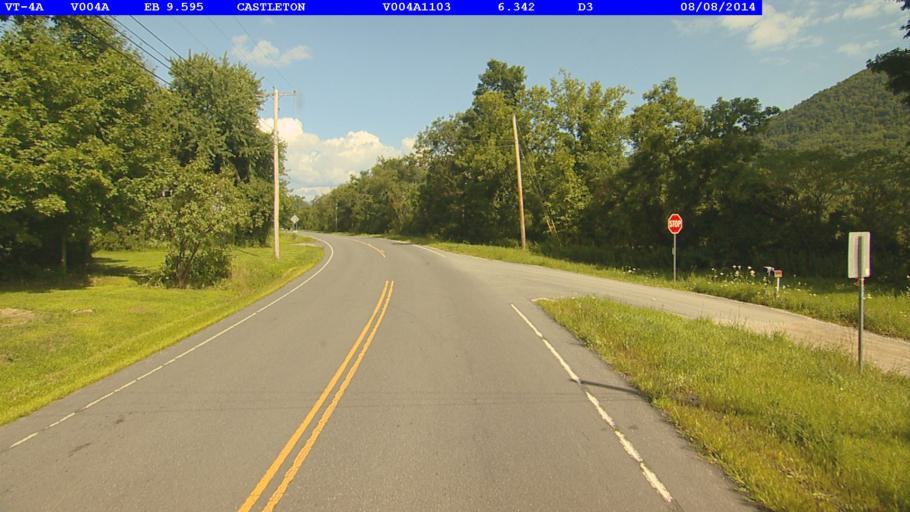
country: US
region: Vermont
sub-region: Rutland County
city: Castleton
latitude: 43.6101
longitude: -73.1242
